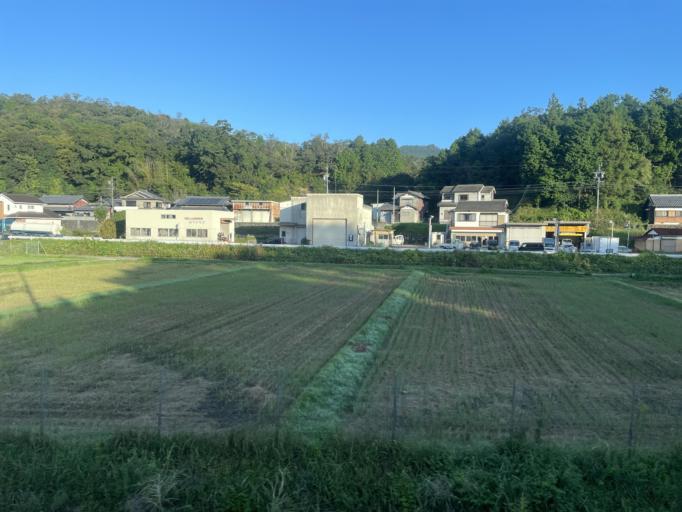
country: JP
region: Mie
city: Nabari
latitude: 34.5873
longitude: 136.0587
